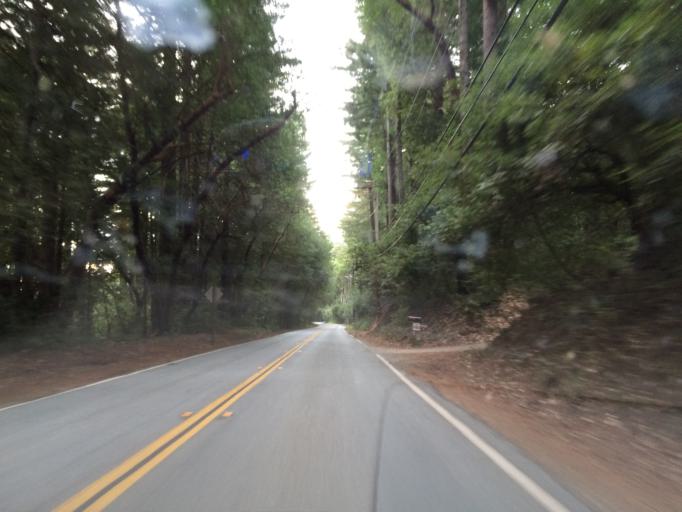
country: US
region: California
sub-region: Santa Cruz County
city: Brookdale
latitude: 37.0904
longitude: -122.1390
